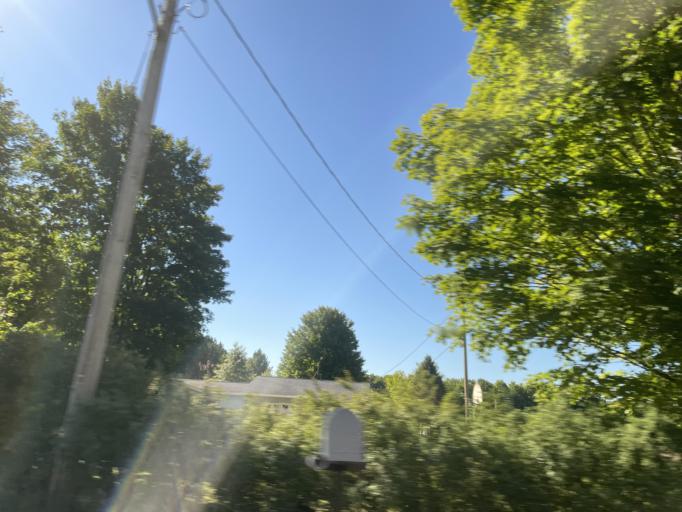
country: US
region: Michigan
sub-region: Benzie County
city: Beulah
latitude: 44.6173
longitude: -86.0547
